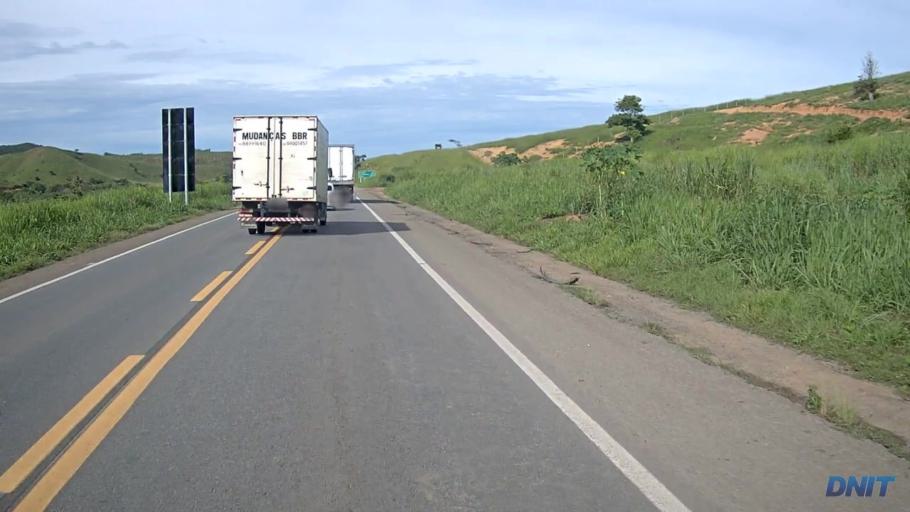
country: BR
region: Minas Gerais
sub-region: Belo Oriente
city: Belo Oriente
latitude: -19.1953
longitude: -42.2806
